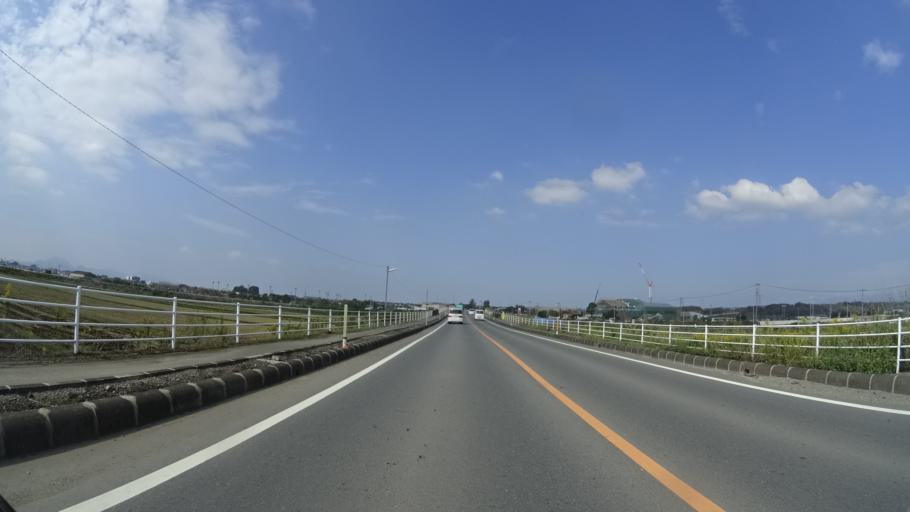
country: JP
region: Kumamoto
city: Ozu
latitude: 32.7817
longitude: 130.8219
